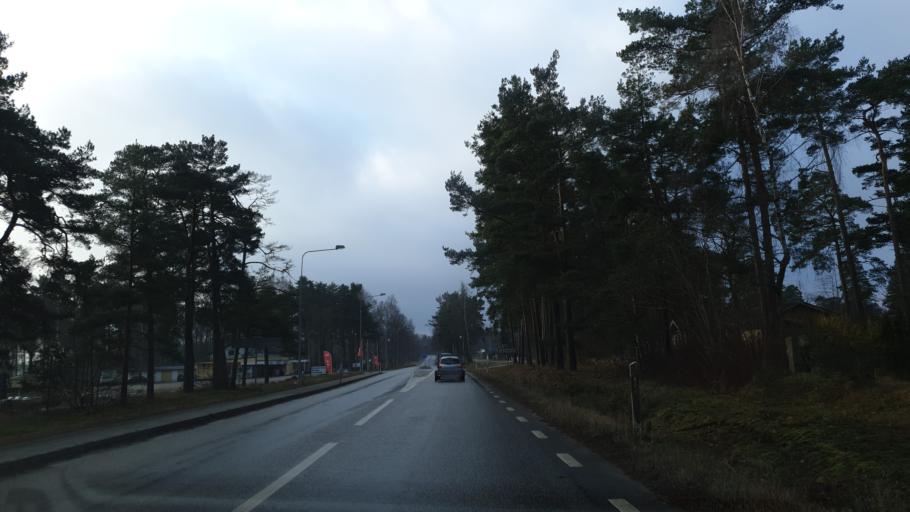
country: SE
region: Blekinge
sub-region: Karlshamns Kommun
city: Morrum
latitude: 56.1543
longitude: 14.6741
